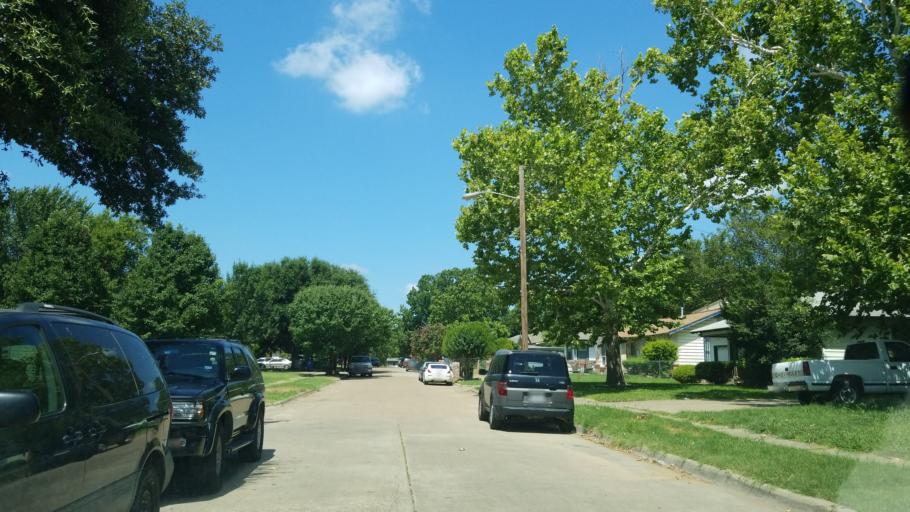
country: US
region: Texas
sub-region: Dallas County
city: Balch Springs
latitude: 32.7373
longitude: -96.6966
